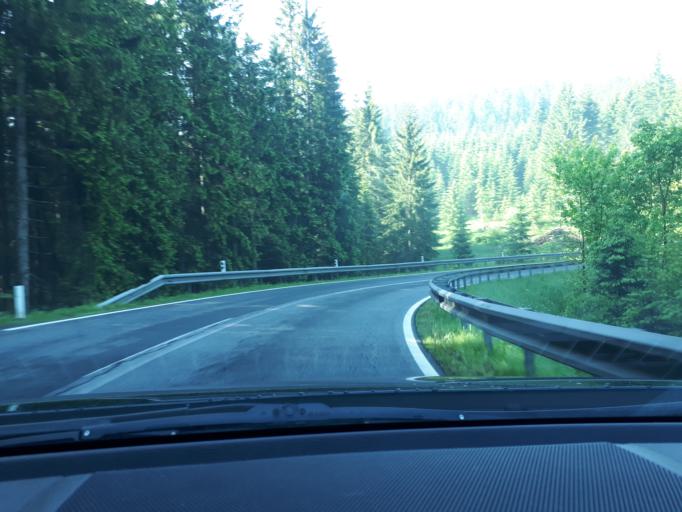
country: AT
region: Styria
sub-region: Politischer Bezirk Voitsberg
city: Pack
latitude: 46.9527
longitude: 14.9808
